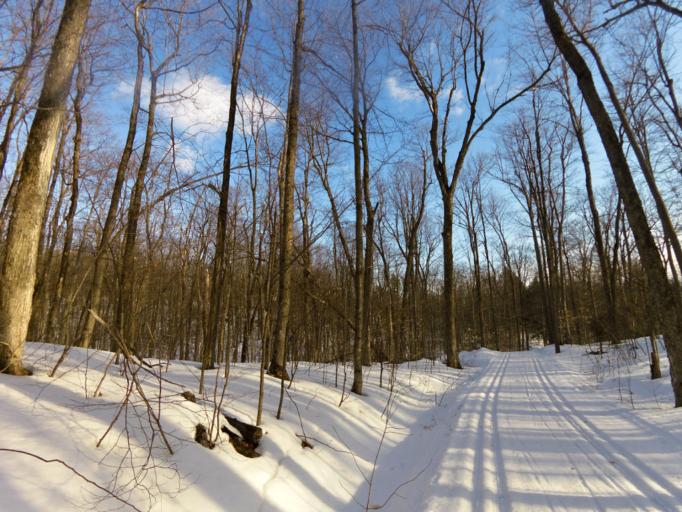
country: CA
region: Quebec
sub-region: Outaouais
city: Gatineau
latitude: 45.4732
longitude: -75.8383
